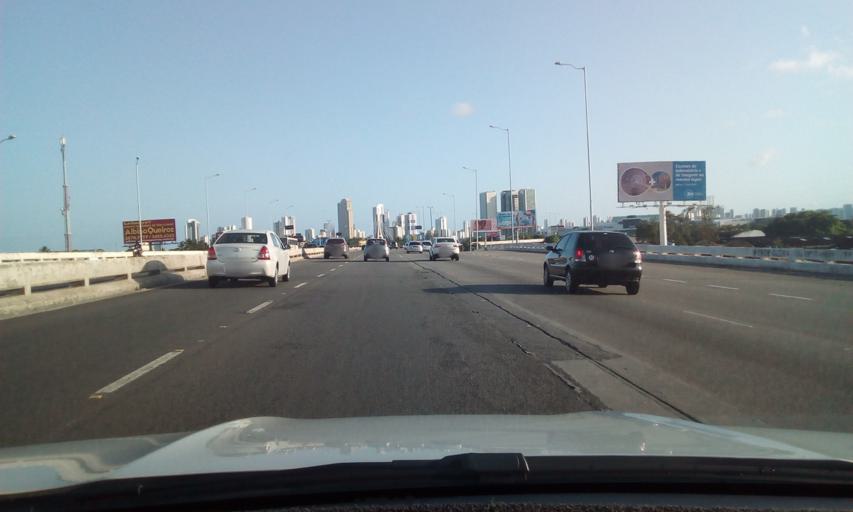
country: BR
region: Pernambuco
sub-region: Recife
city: Recife
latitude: -8.0734
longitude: -34.8940
